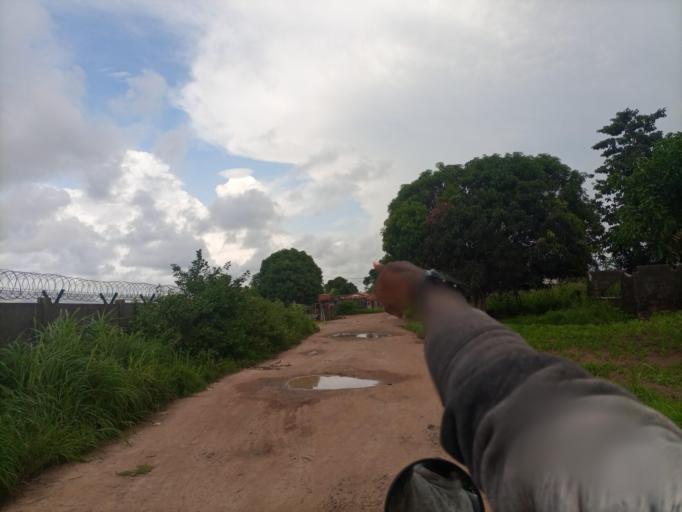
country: SL
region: Northern Province
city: Masoyila
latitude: 8.6104
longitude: -13.1825
